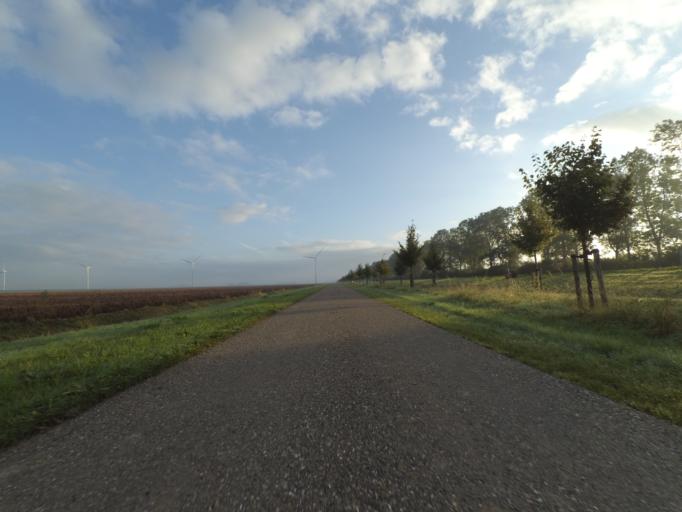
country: NL
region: Flevoland
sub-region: Gemeente Dronten
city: Biddinghuizen
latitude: 52.4441
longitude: 5.6602
